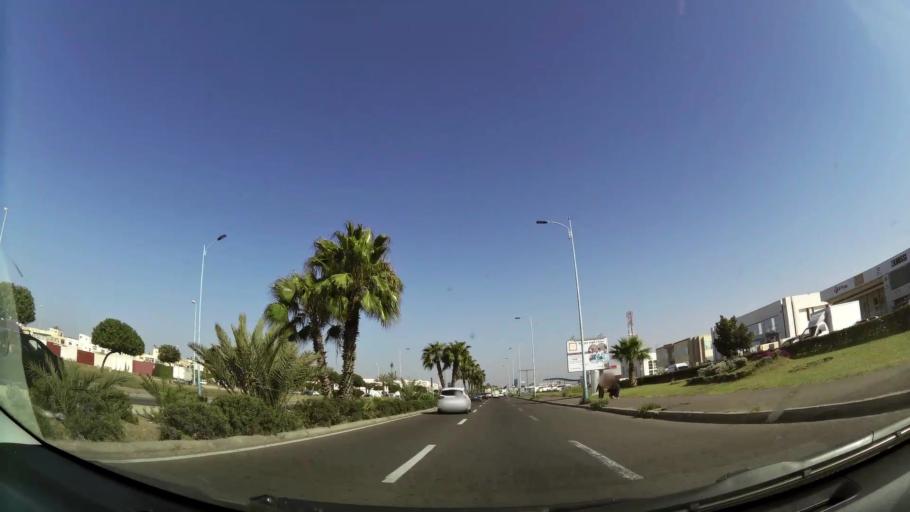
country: MA
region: Souss-Massa-Draa
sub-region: Inezgane-Ait Mellou
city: Inezgane
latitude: 30.3913
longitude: -9.5157
